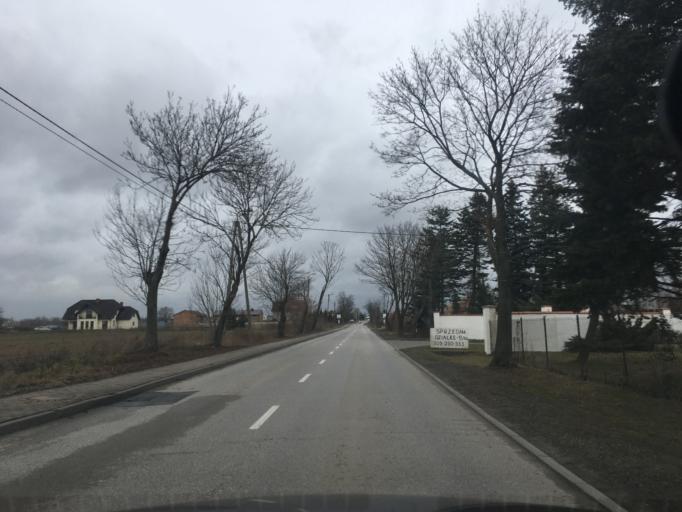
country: PL
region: Masovian Voivodeship
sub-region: Powiat piaseczynski
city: Lesznowola
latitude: 52.1146
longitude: 20.9309
